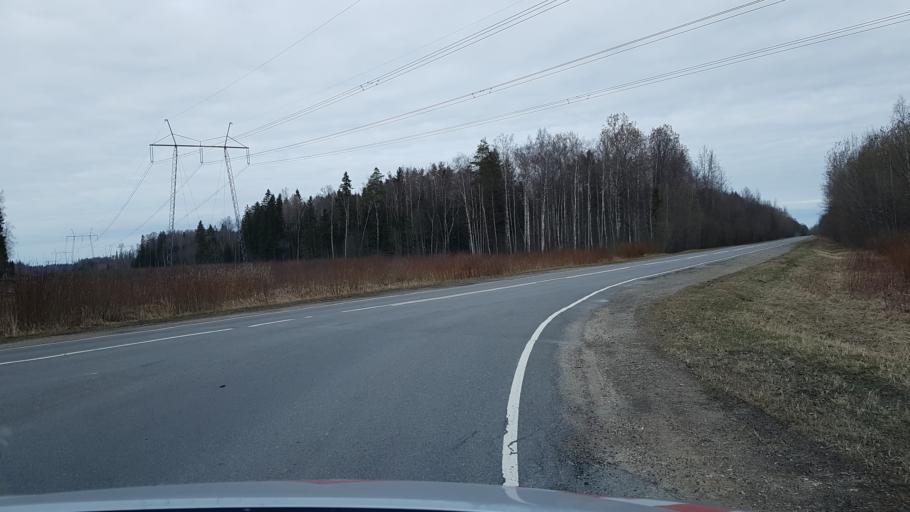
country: EE
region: Ida-Virumaa
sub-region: Sillamaee linn
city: Sillamae
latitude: 59.3525
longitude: 27.7444
